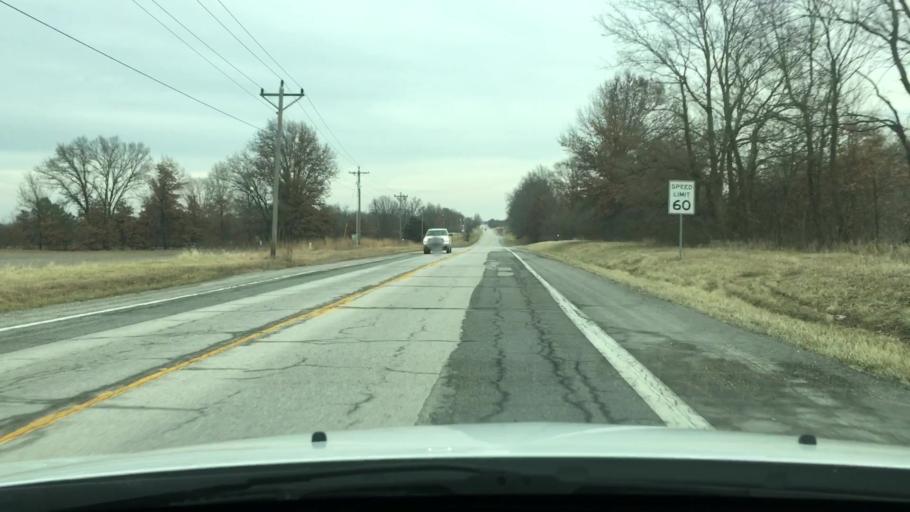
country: US
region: Missouri
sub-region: Audrain County
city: Vandalia
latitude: 39.3468
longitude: -91.4108
